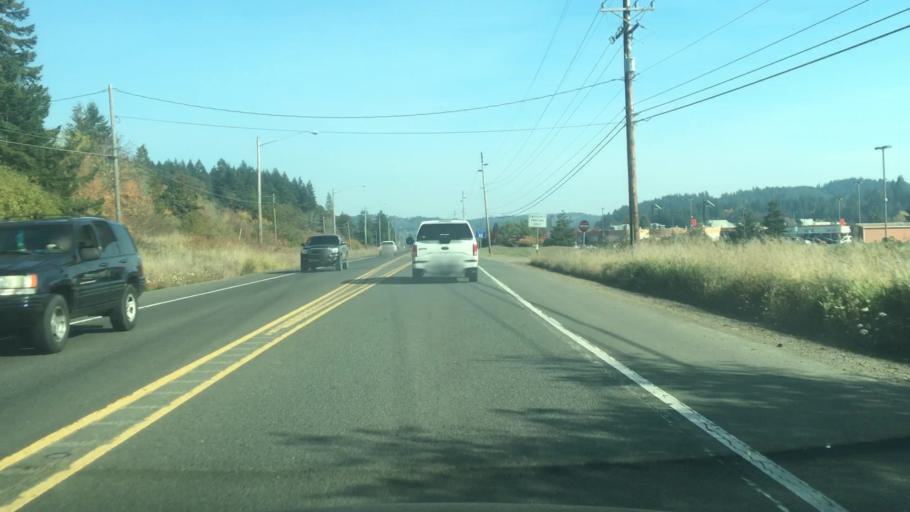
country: US
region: Oregon
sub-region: Polk County
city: Grand Ronde
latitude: 45.0595
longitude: -123.5876
